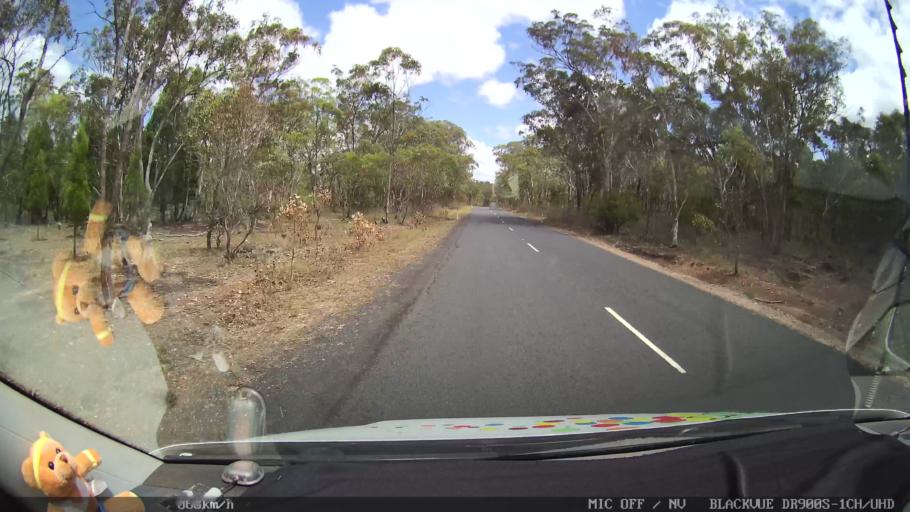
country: AU
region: New South Wales
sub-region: Glen Innes Severn
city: Glen Innes
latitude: -29.4606
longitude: 151.6149
